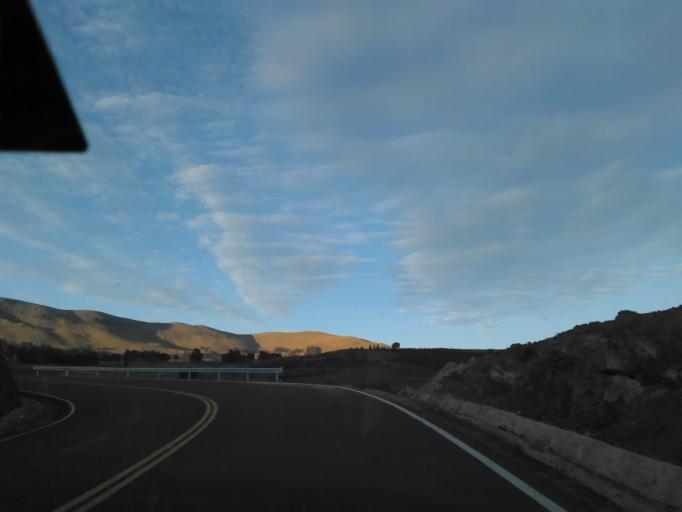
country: BO
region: Cochabamba
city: Arani
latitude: -17.6325
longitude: -65.6210
